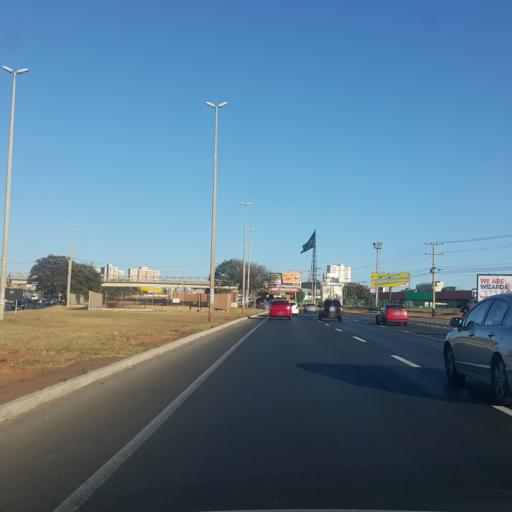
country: BR
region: Federal District
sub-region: Brasilia
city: Brasilia
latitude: -15.8345
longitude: -48.0788
